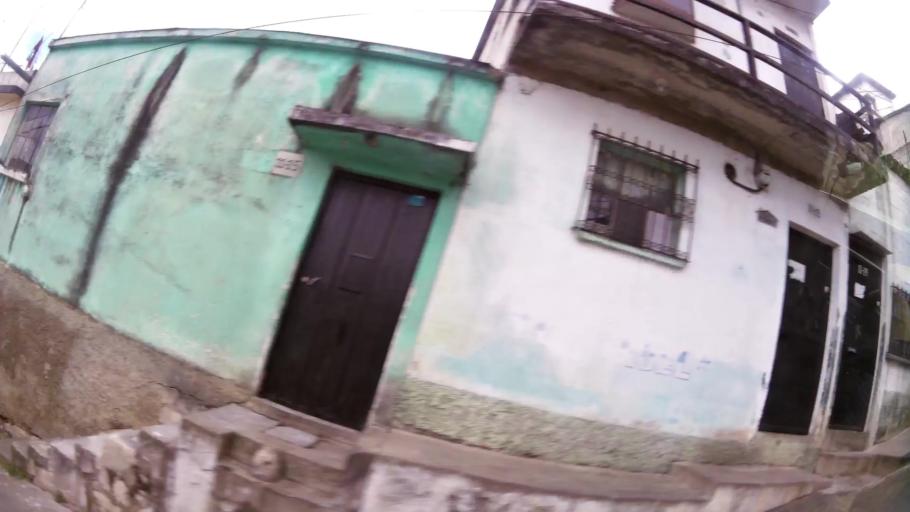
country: GT
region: Guatemala
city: Mixco
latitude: 14.6313
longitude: -90.6096
